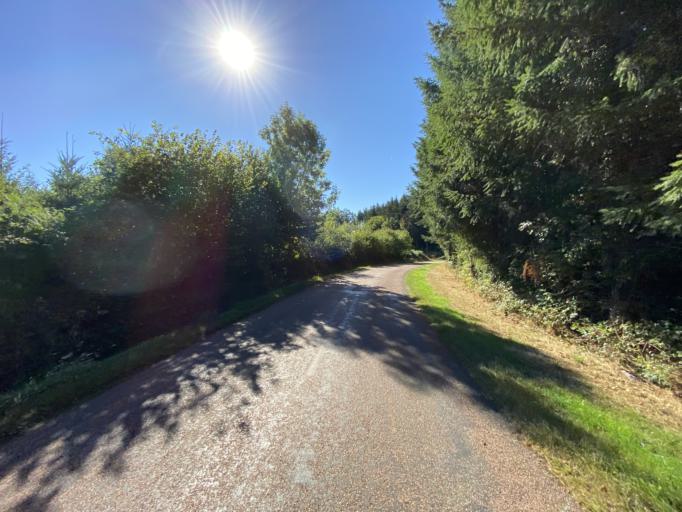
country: FR
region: Bourgogne
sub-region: Departement de la Cote-d'Or
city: Saulieu
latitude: 47.2567
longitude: 4.1860
